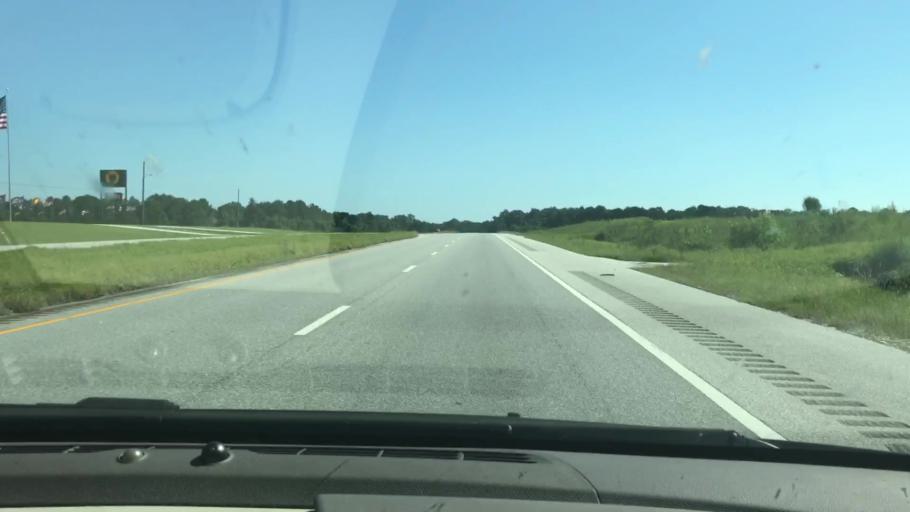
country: US
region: Alabama
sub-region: Russell County
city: Ladonia
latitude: 32.3606
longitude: -85.1051
